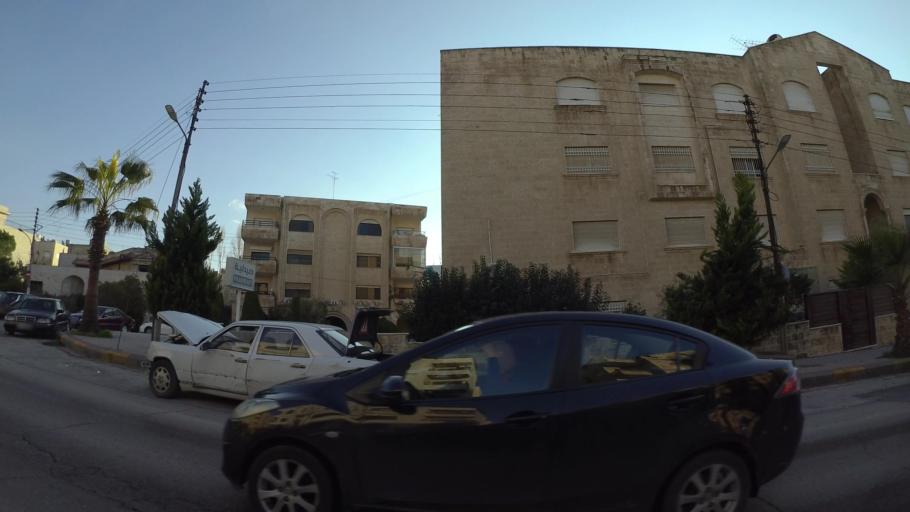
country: JO
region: Amman
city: Al Jubayhah
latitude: 31.9754
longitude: 35.8724
